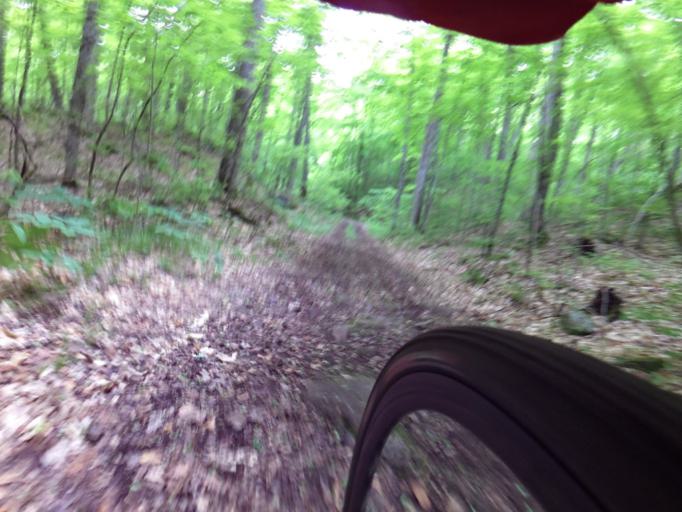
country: CA
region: Ontario
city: Arnprior
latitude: 45.1796
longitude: -76.5333
